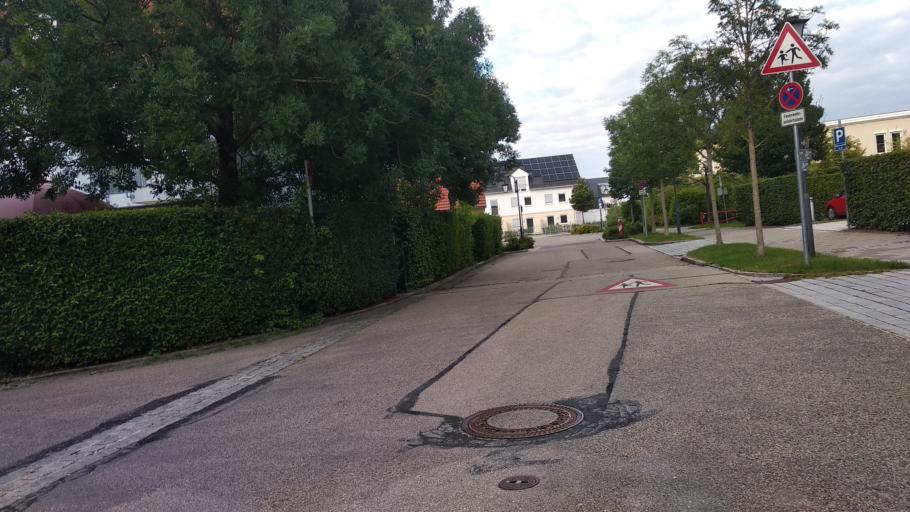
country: DE
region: Bavaria
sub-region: Upper Bavaria
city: Aschheim
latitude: 48.1705
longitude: 11.7226
